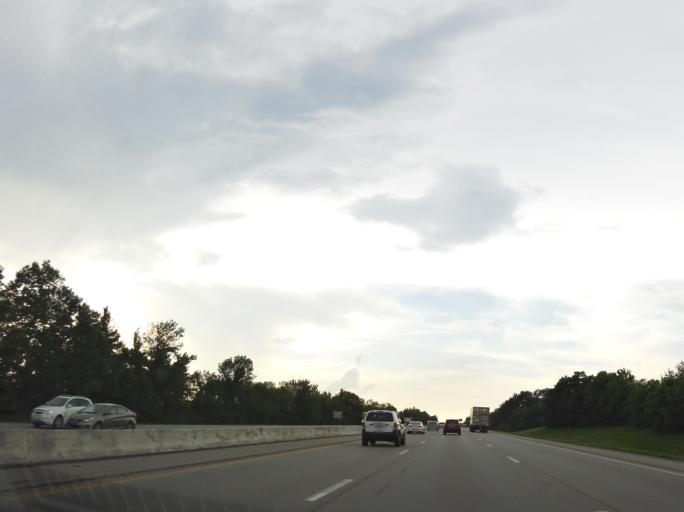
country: US
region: Kentucky
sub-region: Fayette County
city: Lexington
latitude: 37.9858
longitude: -84.3911
